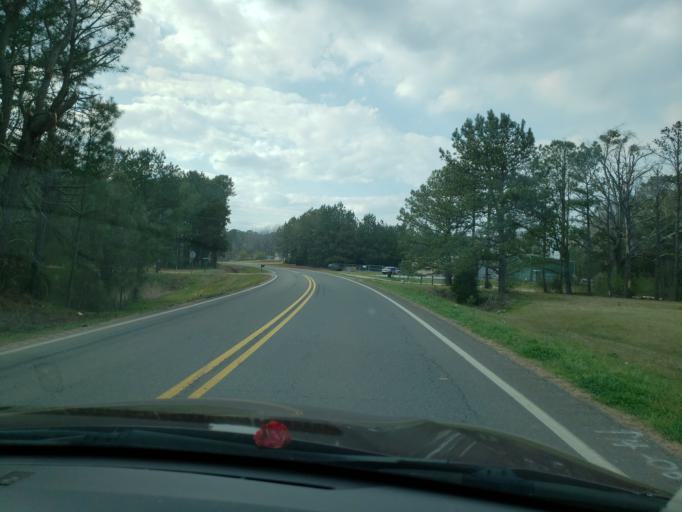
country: US
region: Alabama
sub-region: Hale County
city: Greensboro
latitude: 32.7209
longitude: -87.6223
